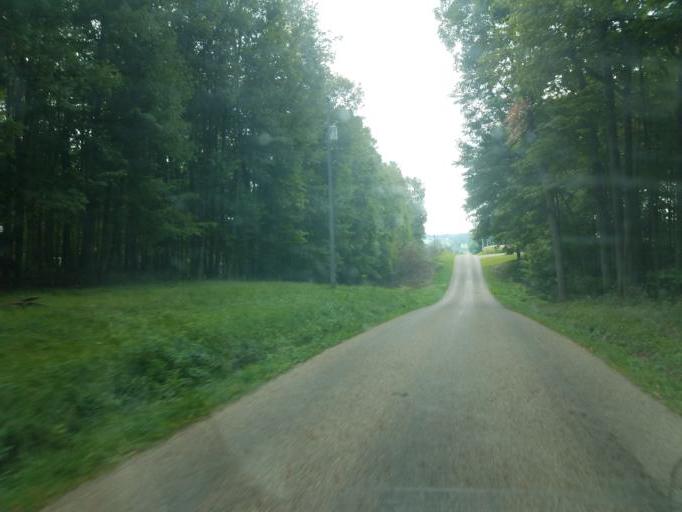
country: US
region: Ohio
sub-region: Knox County
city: Gambier
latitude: 40.3553
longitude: -82.3478
